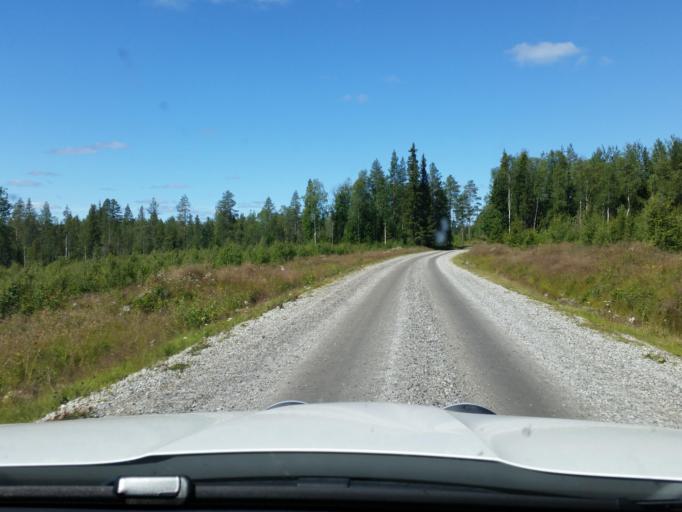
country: SE
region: Vaesterbotten
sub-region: Skelleftea Kommun
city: Storvik
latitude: 65.2443
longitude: 20.7249
